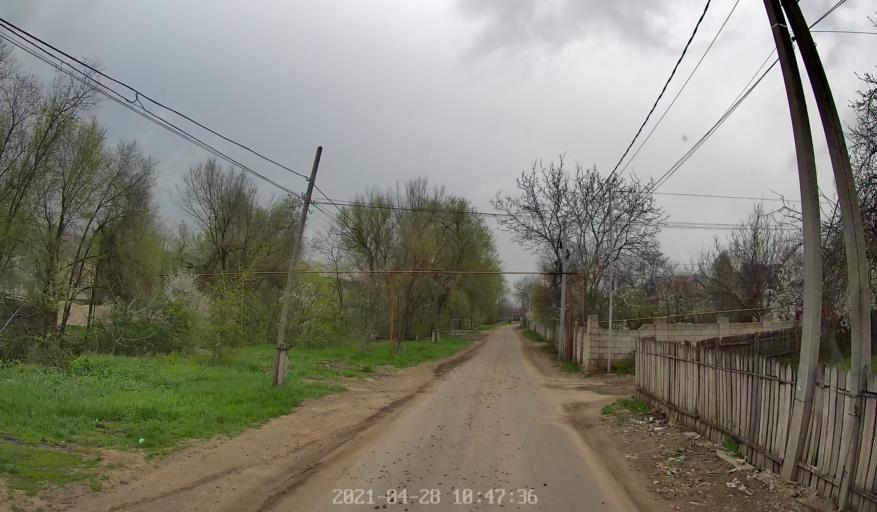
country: MD
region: Chisinau
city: Singera
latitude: 46.9881
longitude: 28.9476
